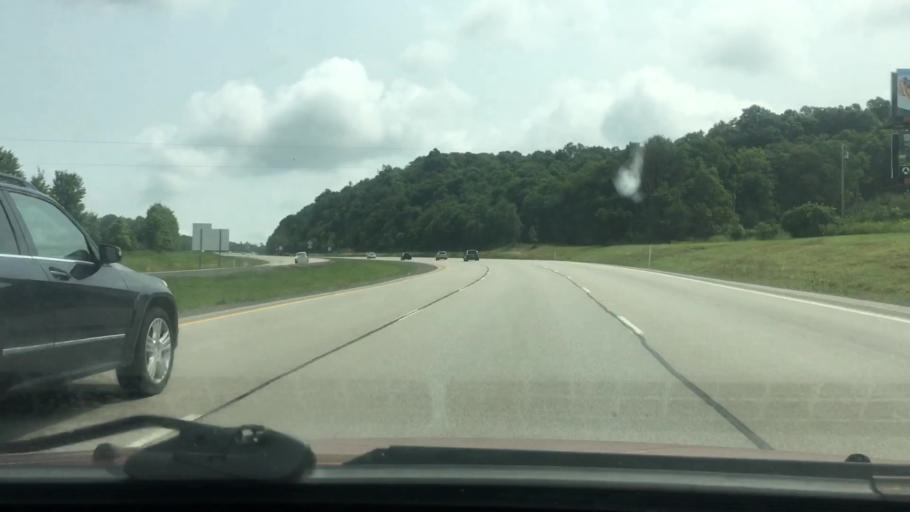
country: US
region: West Virginia
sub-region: Preston County
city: Terra Alta
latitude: 39.6574
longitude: -79.5124
